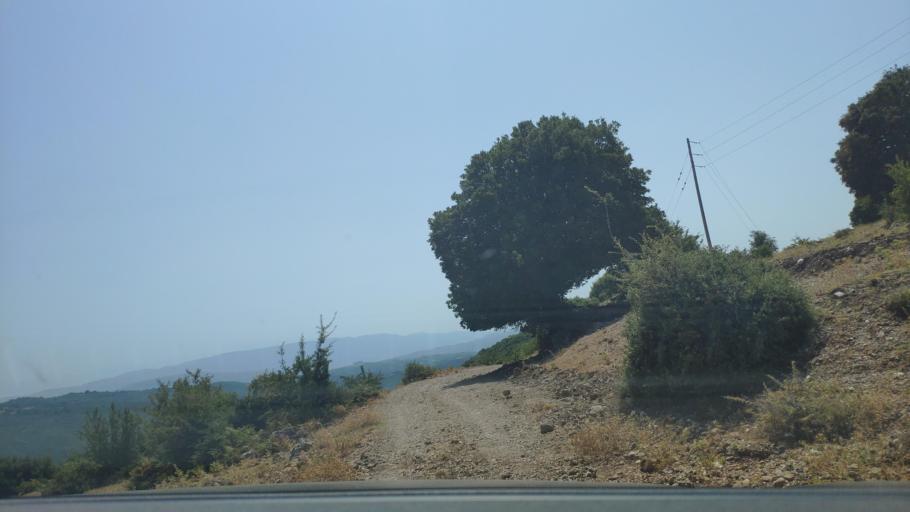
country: GR
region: West Greece
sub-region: Nomos Aitolias kai Akarnanias
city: Monastirakion
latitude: 38.8163
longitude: 21.0246
